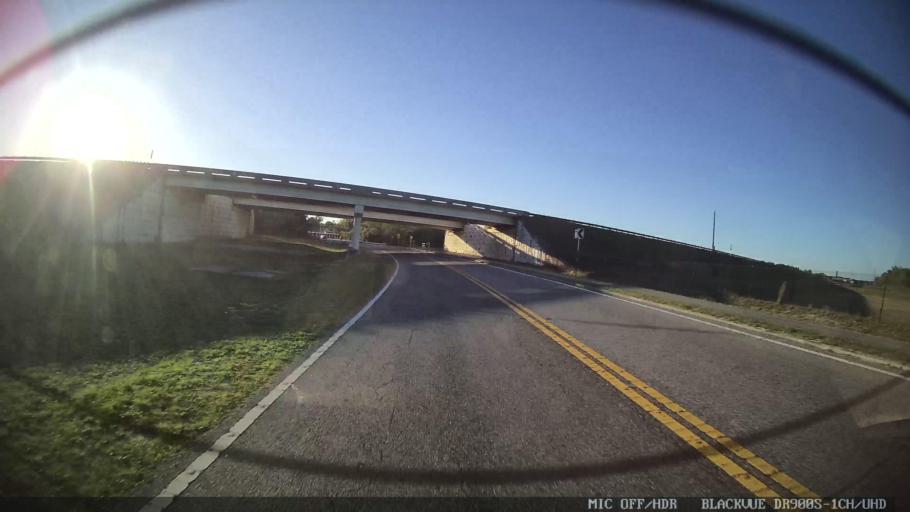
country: US
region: Florida
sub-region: Pasco County
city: Shady Hills
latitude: 28.3709
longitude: -82.5420
